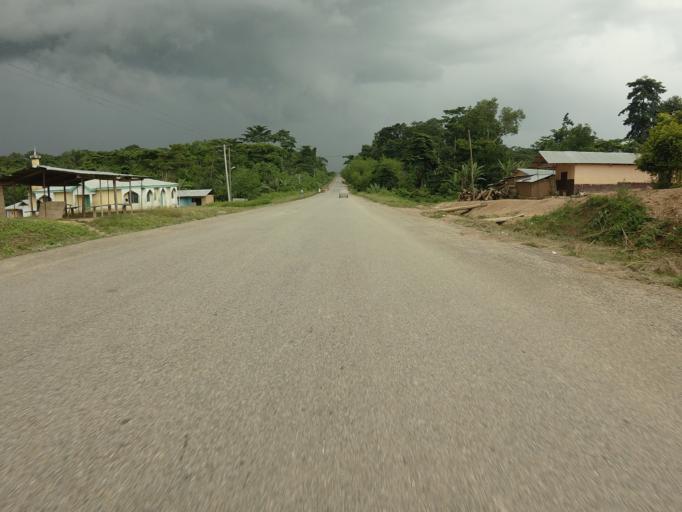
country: TG
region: Plateaux
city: Badou
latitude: 7.6709
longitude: 0.5194
